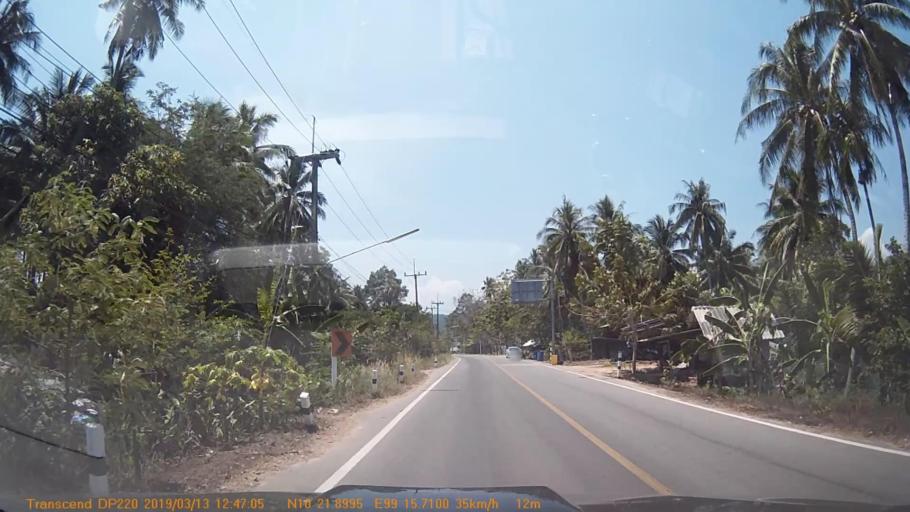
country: TH
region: Chumphon
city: Chumphon
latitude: 10.3648
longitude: 99.2619
